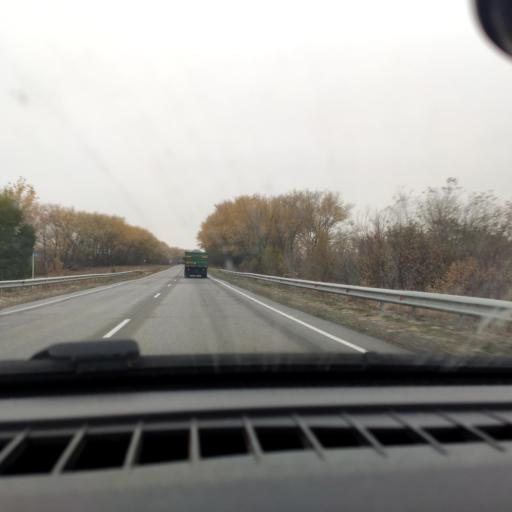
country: RU
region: Voronezj
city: Ostrogozhsk
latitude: 50.9704
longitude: 39.0023
